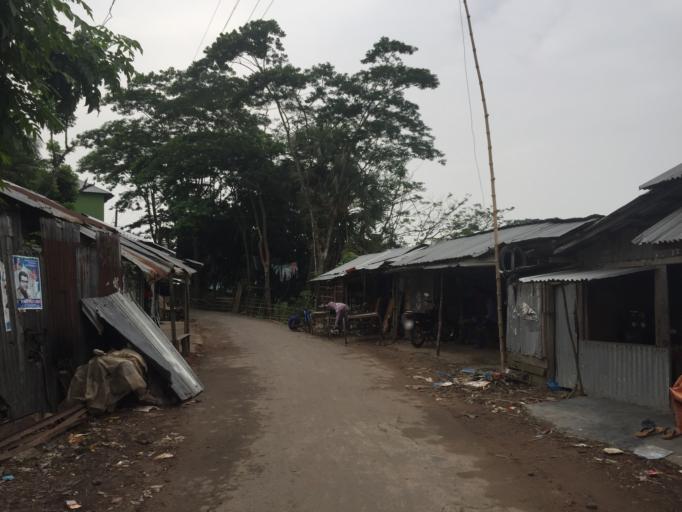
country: BD
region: Barisal
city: Mathba
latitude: 22.2169
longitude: 89.9176
